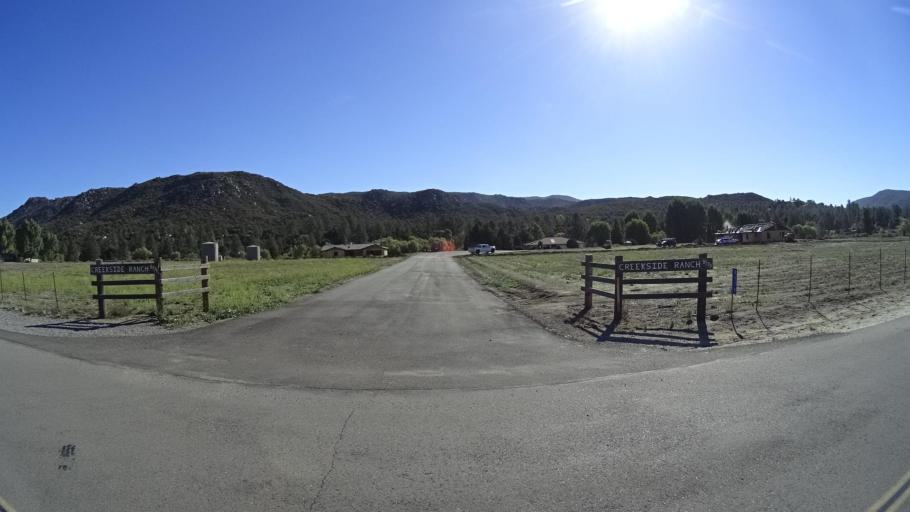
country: US
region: California
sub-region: San Diego County
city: Pine Valley
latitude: 32.8398
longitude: -116.5304
